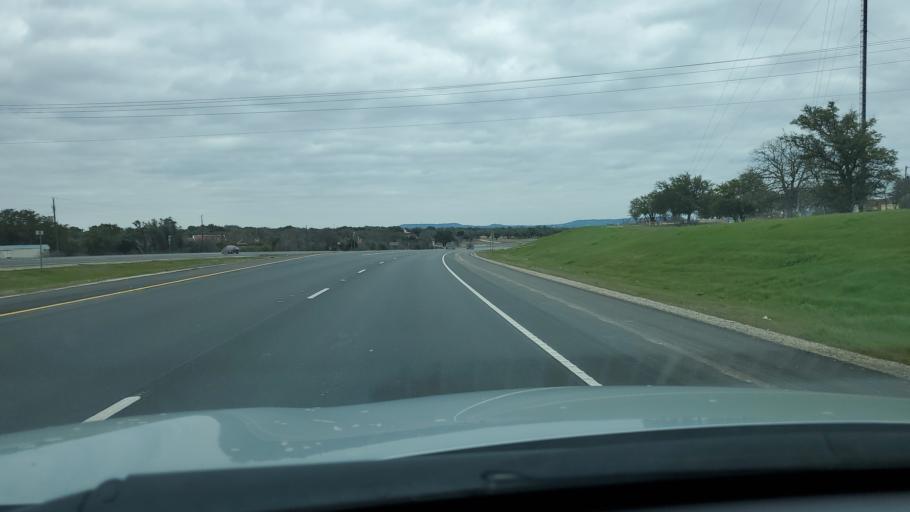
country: US
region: Texas
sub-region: Williamson County
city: Florence
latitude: 30.9341
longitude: -97.7918
